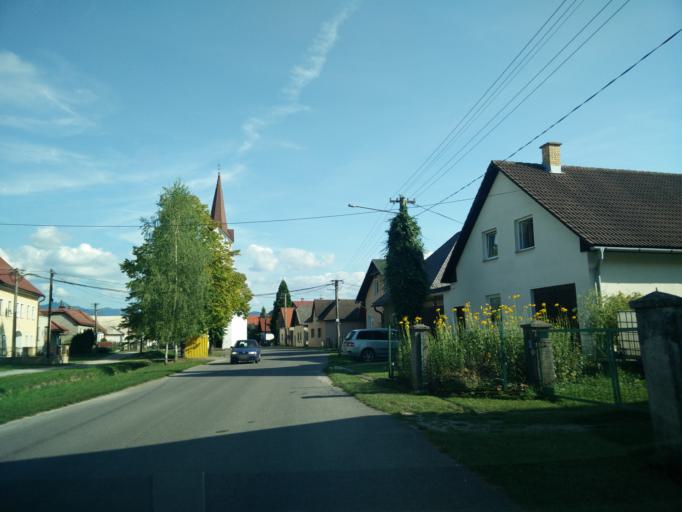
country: SK
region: Zilinsky
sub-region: Okres Martin
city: Martin
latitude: 48.9726
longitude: 18.8215
